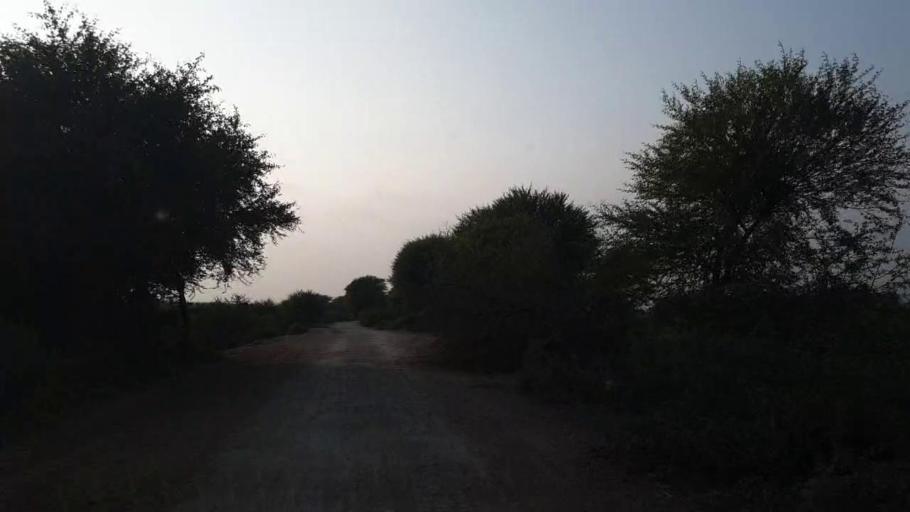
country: PK
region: Sindh
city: Tando Ghulam Ali
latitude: 25.0526
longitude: 68.9619
